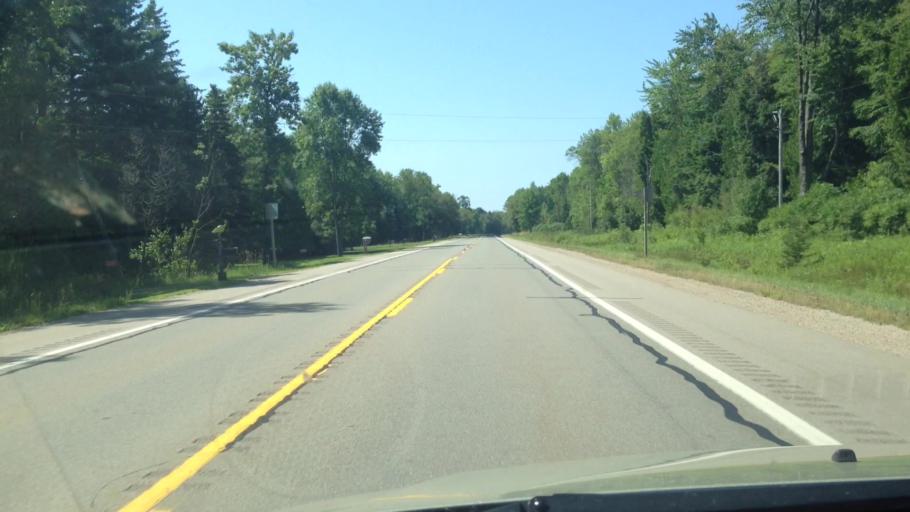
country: US
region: Michigan
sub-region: Menominee County
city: Menominee
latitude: 45.2702
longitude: -87.4694
